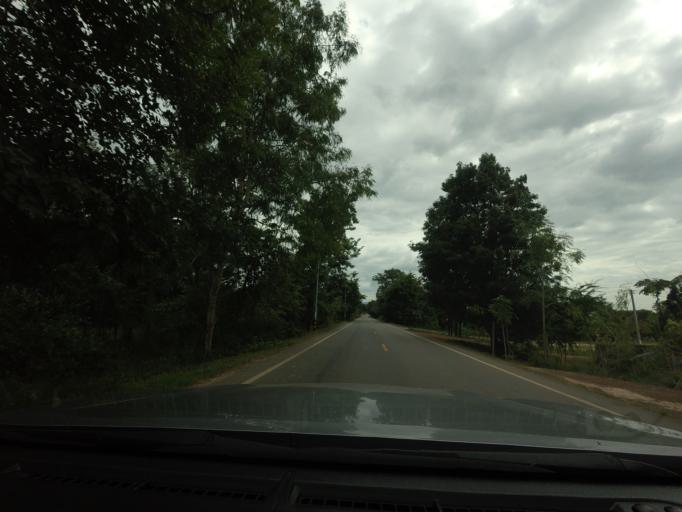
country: TH
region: Phitsanulok
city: Noen Maprang
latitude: 16.7037
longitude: 100.5868
